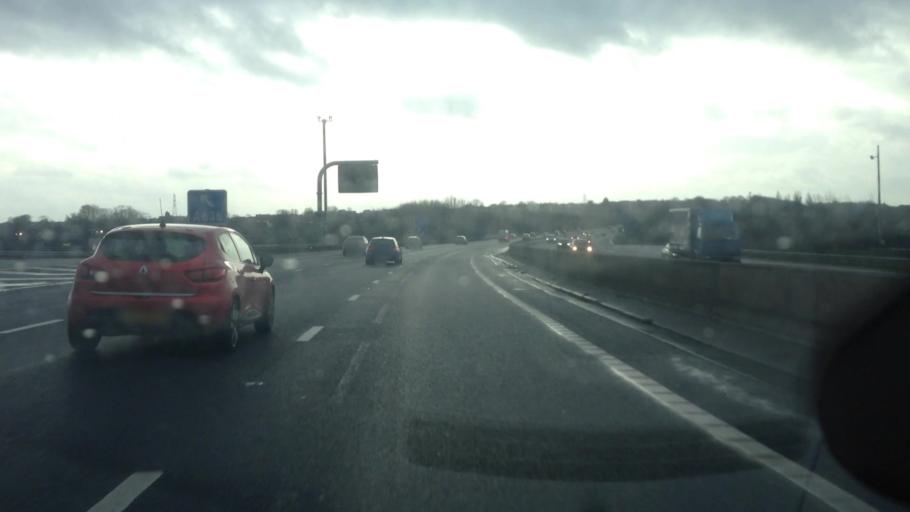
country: GB
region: England
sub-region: City and Borough of Wakefield
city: Crigglestone
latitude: 53.6539
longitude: -1.5279
